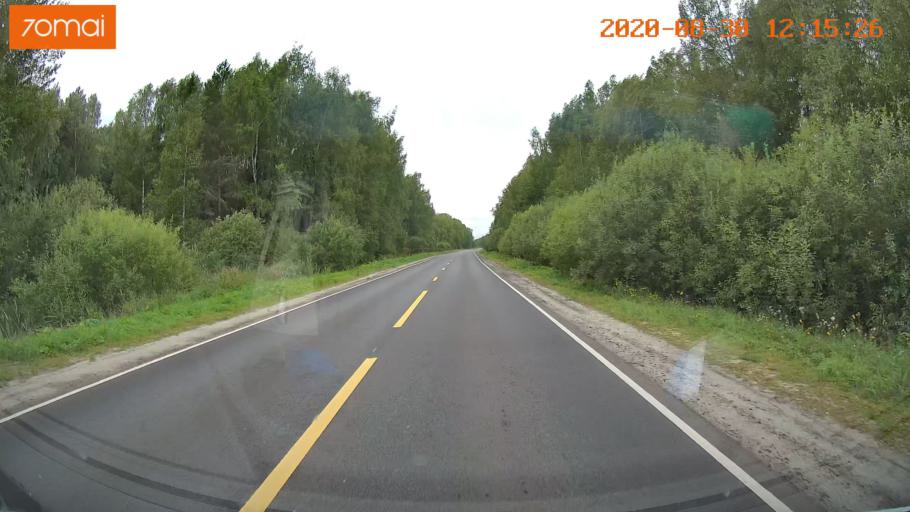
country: RU
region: Ivanovo
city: Yur'yevets
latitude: 57.3172
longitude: 43.0299
